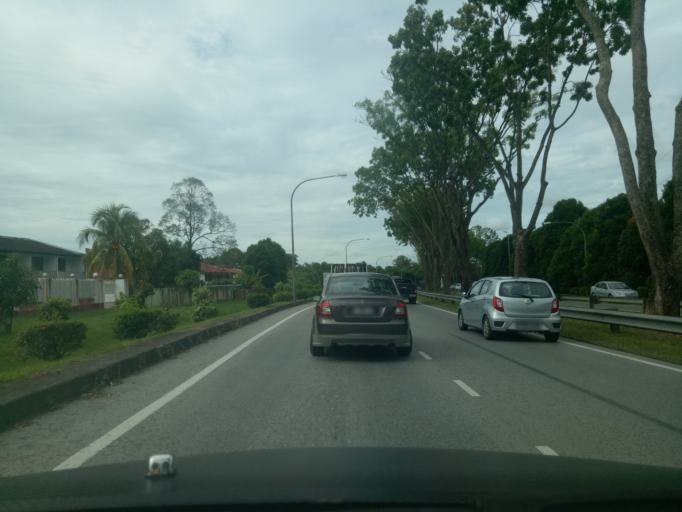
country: MY
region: Sarawak
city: Kuching
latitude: 1.5439
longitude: 110.3729
